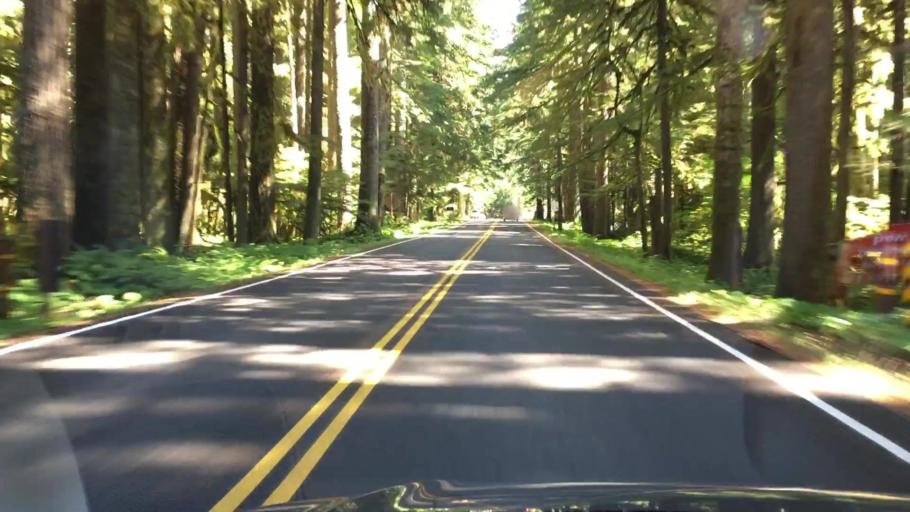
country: US
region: Washington
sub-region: Pierce County
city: Eatonville
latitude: 46.7423
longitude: -121.8988
